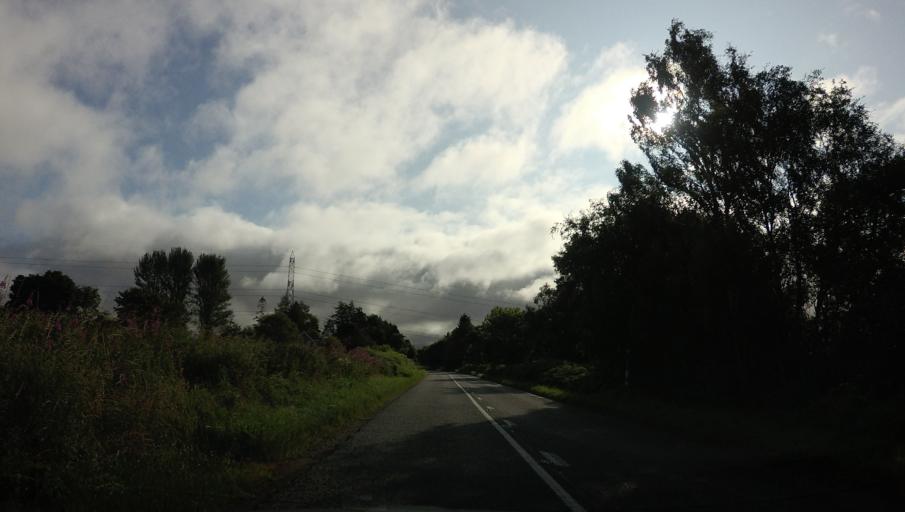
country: GB
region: Scotland
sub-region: Aberdeenshire
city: Banchory
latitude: 57.0631
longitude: -2.3936
